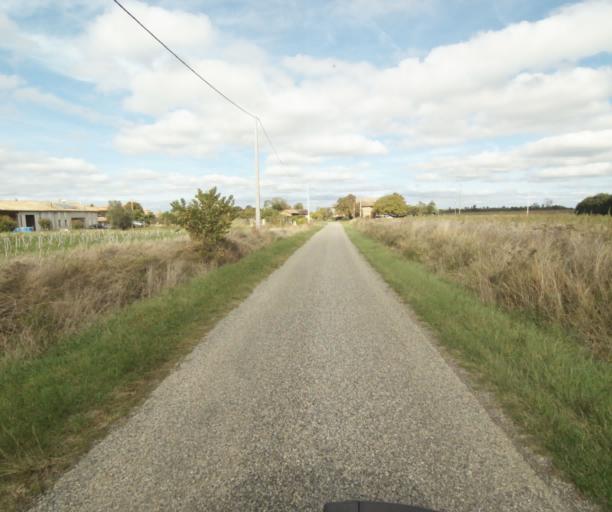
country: FR
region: Midi-Pyrenees
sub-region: Departement du Tarn-et-Garonne
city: Saint-Porquier
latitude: 43.9524
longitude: 1.1522
